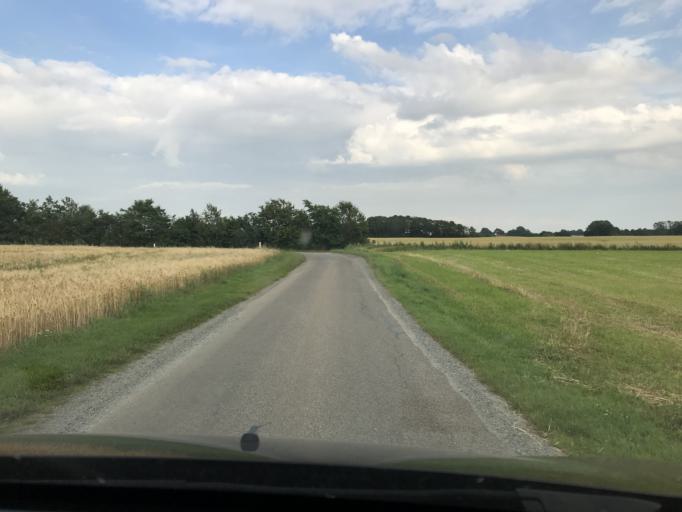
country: DK
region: South Denmark
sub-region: Vejle Kommune
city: Jelling
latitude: 55.8032
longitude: 9.4008
